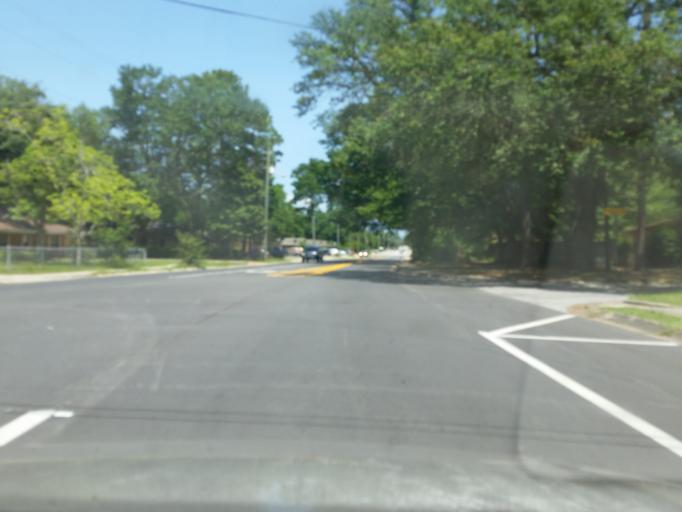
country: US
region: Florida
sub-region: Escambia County
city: Ferry Pass
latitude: 30.4884
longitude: -87.2124
